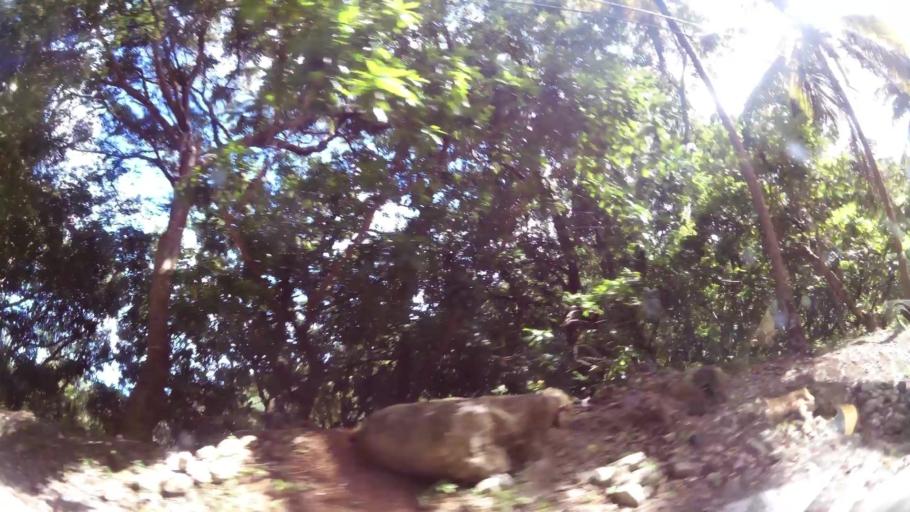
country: DM
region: Saint John
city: Portsmouth
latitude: 15.6260
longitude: -61.4149
